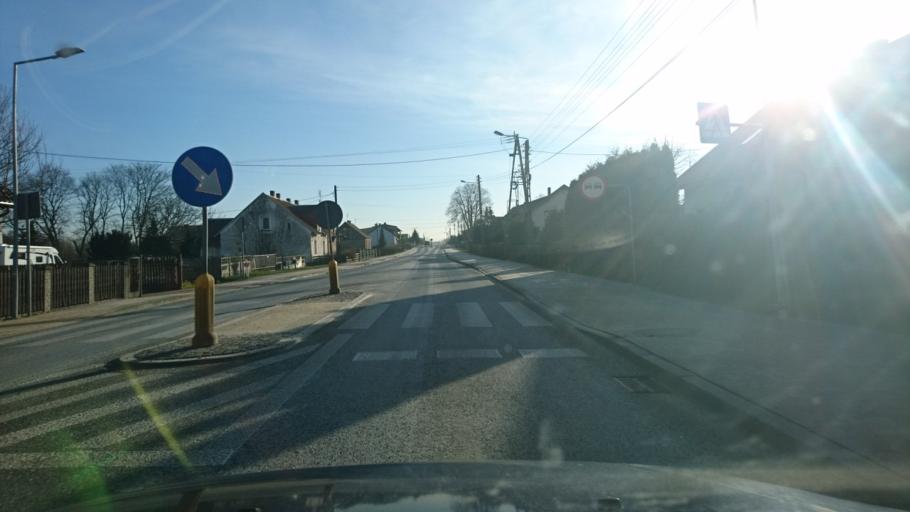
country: PL
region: Silesian Voivodeship
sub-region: Powiat klobucki
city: Starokrzepice
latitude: 51.0167
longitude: 18.6535
